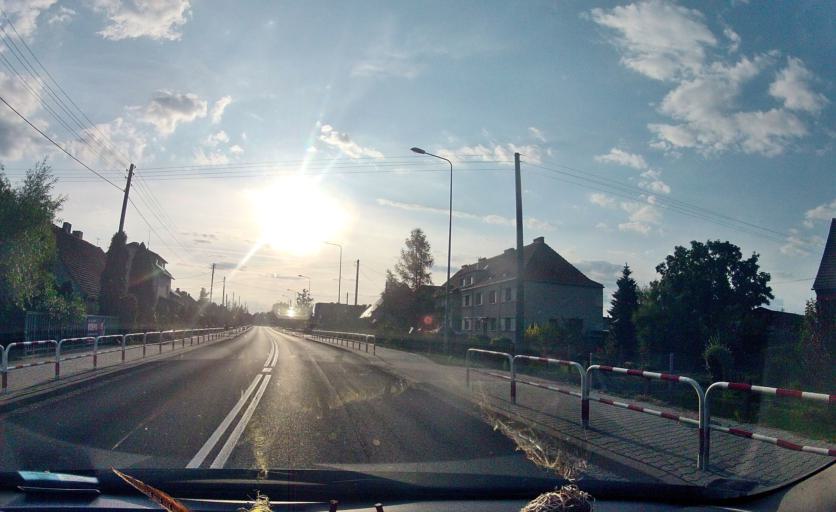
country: PL
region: Opole Voivodeship
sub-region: Powiat kluczborski
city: Kluczbork
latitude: 50.9748
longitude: 18.2334
